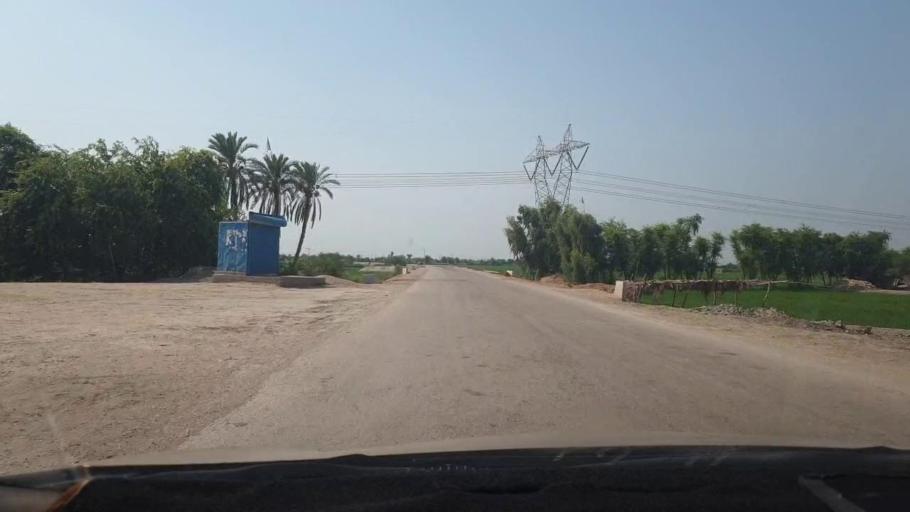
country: PK
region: Sindh
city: Larkana
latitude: 27.6072
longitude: 68.2399
